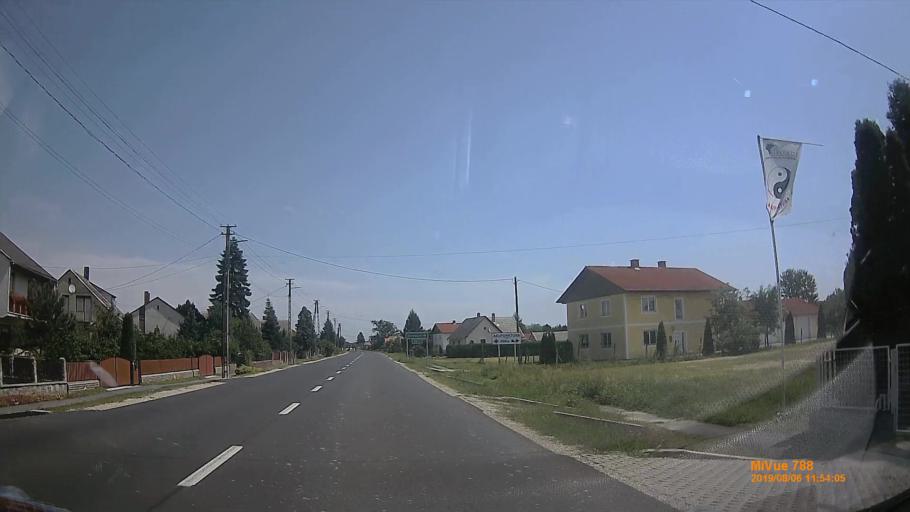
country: HU
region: Vas
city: Kormend
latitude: 47.0445
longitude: 16.6728
